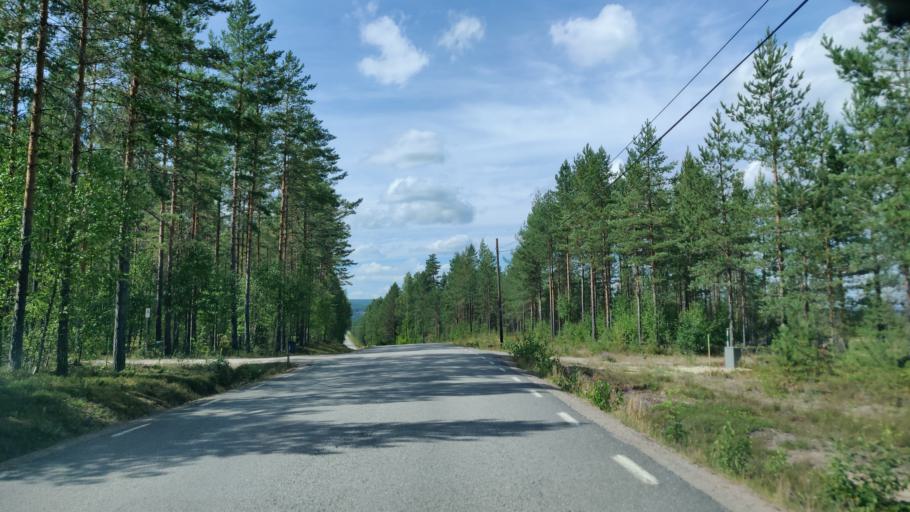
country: SE
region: Vaermland
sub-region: Hagfors Kommun
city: Ekshaerad
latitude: 60.0725
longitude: 13.5255
